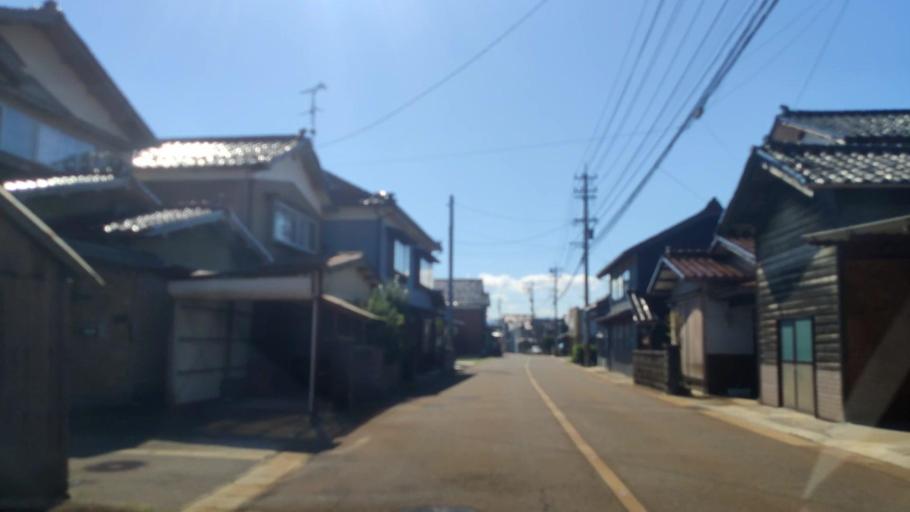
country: JP
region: Ishikawa
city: Nanao
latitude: 37.4391
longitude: 137.2701
